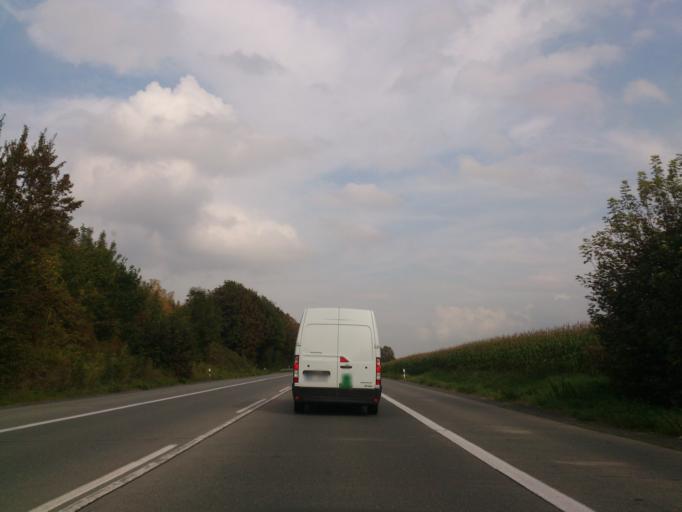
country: DE
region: North Rhine-Westphalia
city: Geseke
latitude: 51.6361
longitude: 8.4881
